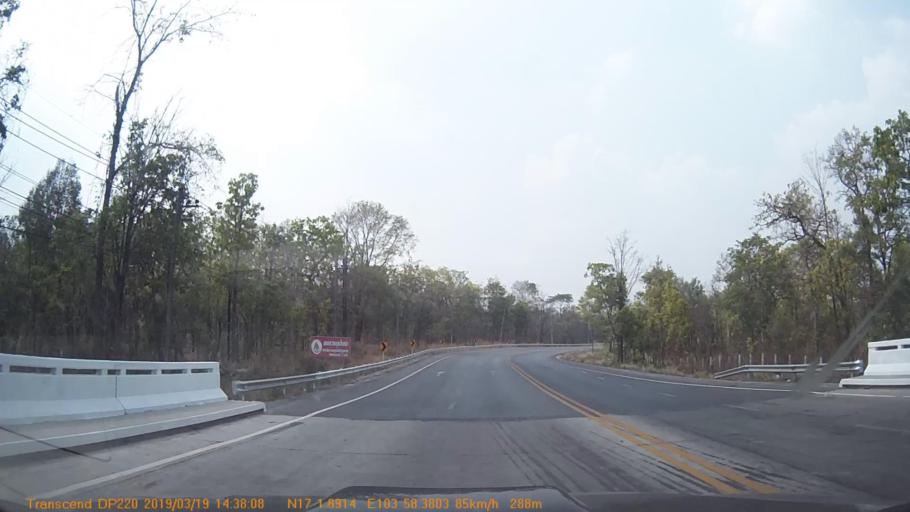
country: TH
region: Sakon Nakhon
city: Phu Phan
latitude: 17.0317
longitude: 103.9728
